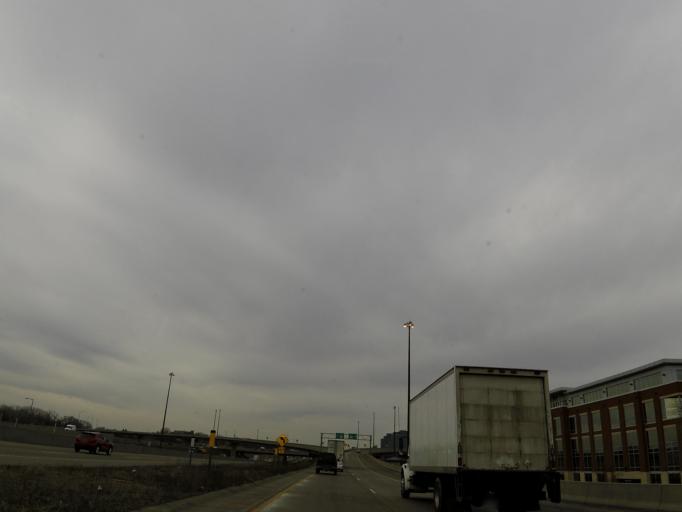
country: US
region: Minnesota
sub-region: Hennepin County
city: Edina
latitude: 44.8598
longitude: -93.3891
